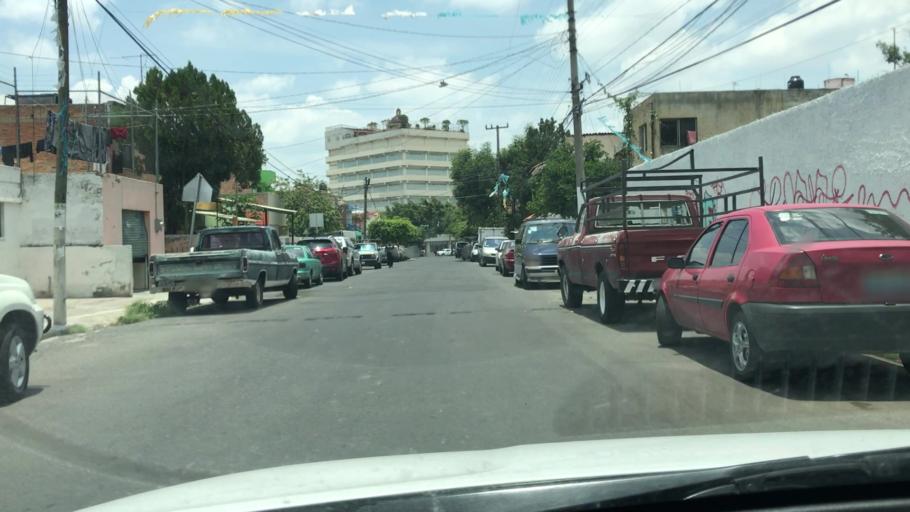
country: MX
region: Jalisco
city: Zapopan2
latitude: 20.7305
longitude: -103.4056
